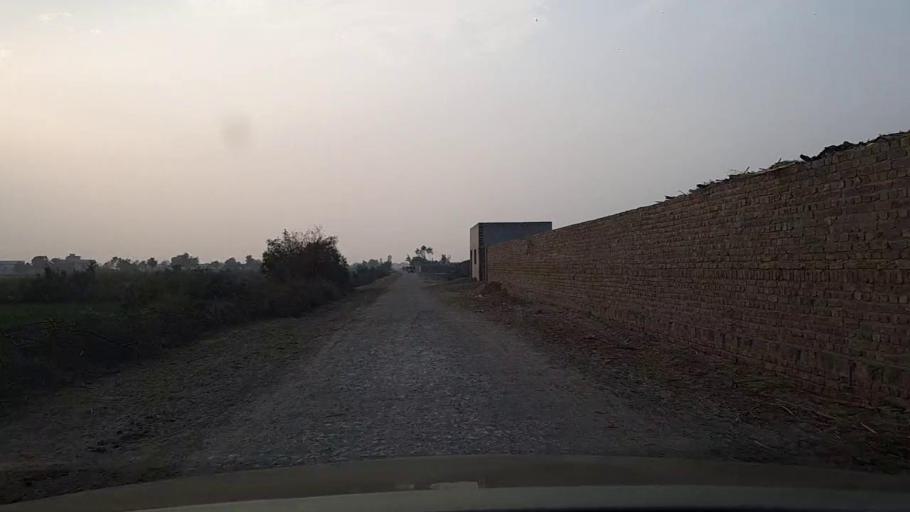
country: PK
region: Sindh
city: Sanghar
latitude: 26.1857
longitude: 68.9513
